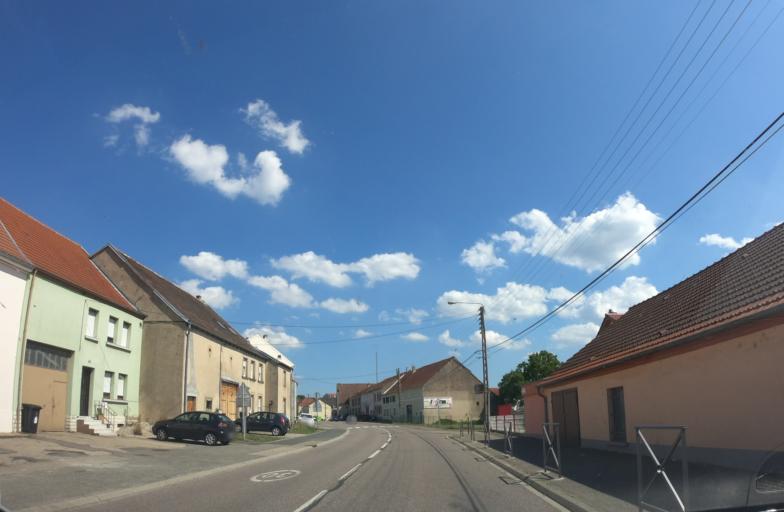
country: FR
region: Lorraine
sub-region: Departement de la Moselle
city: Hundling
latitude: 49.1069
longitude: 6.9787
